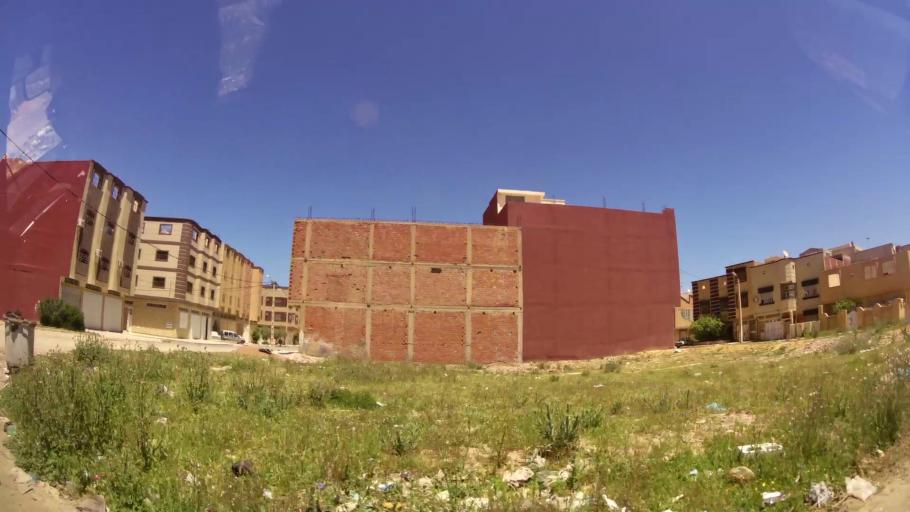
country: MA
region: Oriental
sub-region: Oujda-Angad
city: Oujda
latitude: 34.6743
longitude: -1.8790
